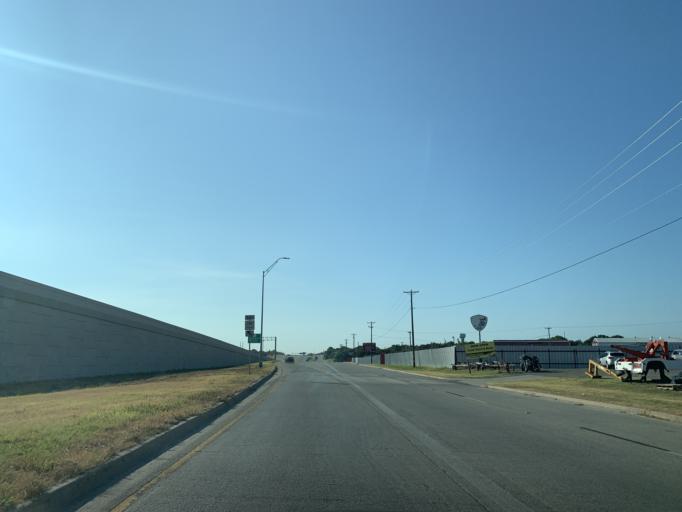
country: US
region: Texas
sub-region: Tarrant County
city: Lakeside
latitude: 32.8371
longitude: -97.4915
